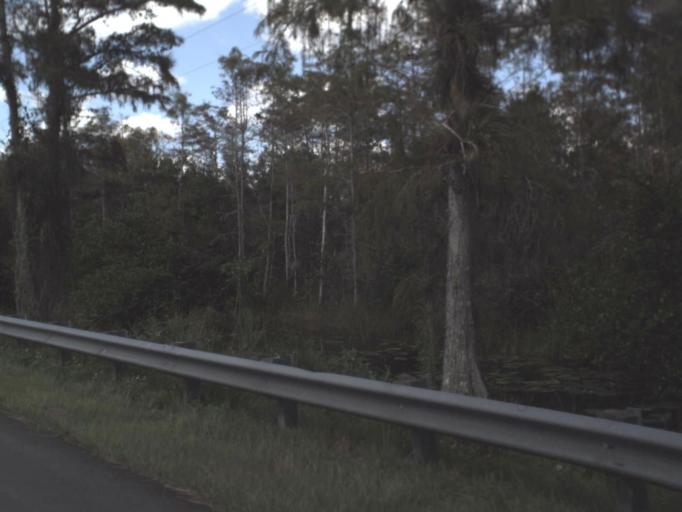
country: US
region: Florida
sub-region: Miami-Dade County
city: Kendall West
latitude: 25.8344
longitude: -80.9068
